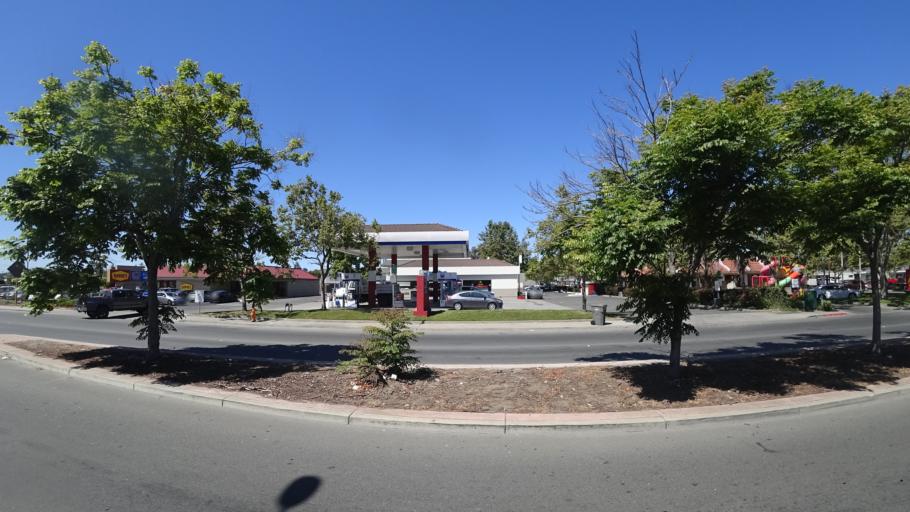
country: US
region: California
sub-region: Alameda County
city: Union City
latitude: 37.6087
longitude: -122.0656
